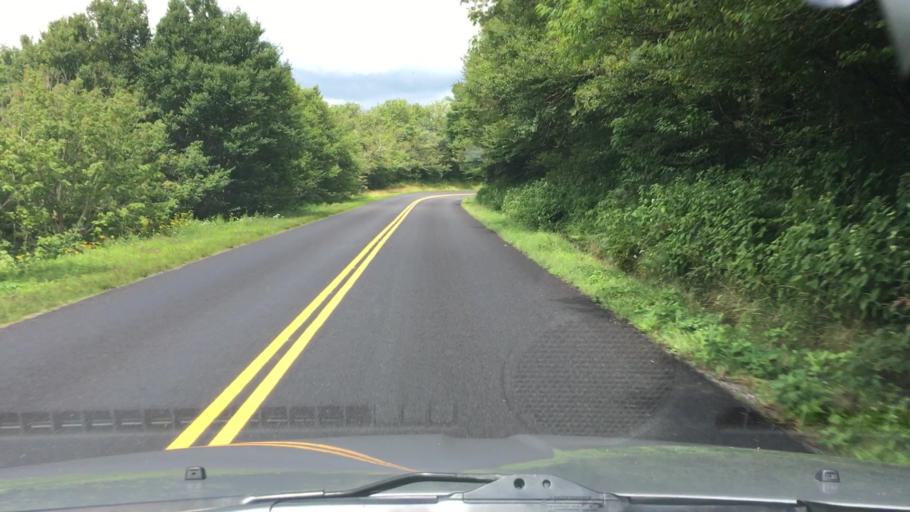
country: US
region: North Carolina
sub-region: Buncombe County
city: Black Mountain
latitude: 35.7172
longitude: -82.3606
